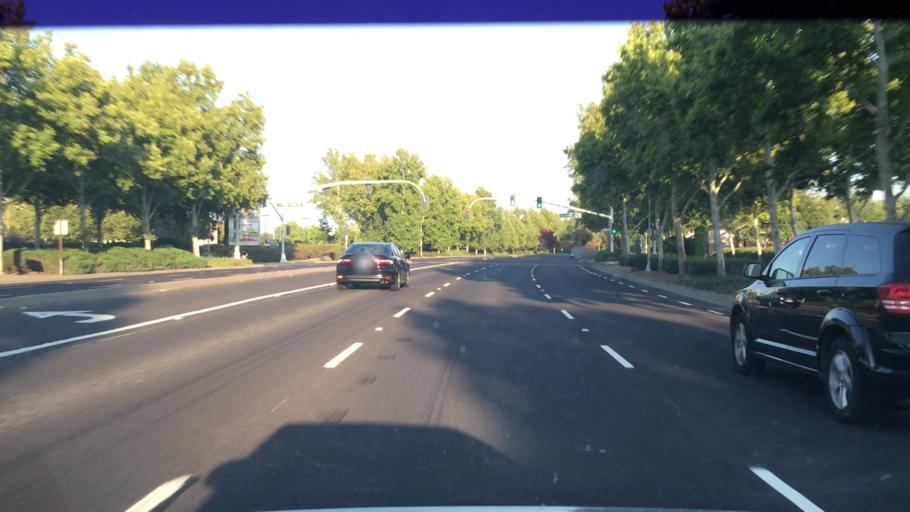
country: US
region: California
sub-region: Sacramento County
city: Laguna
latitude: 38.4275
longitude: -121.4666
